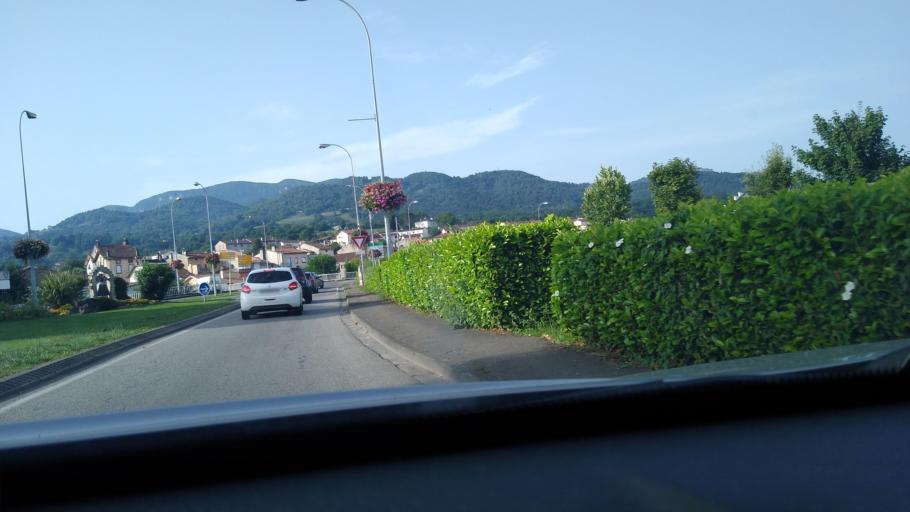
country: FR
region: Midi-Pyrenees
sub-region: Departement de l'Ariege
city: Saint-Girons
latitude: 42.9866
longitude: 1.1402
